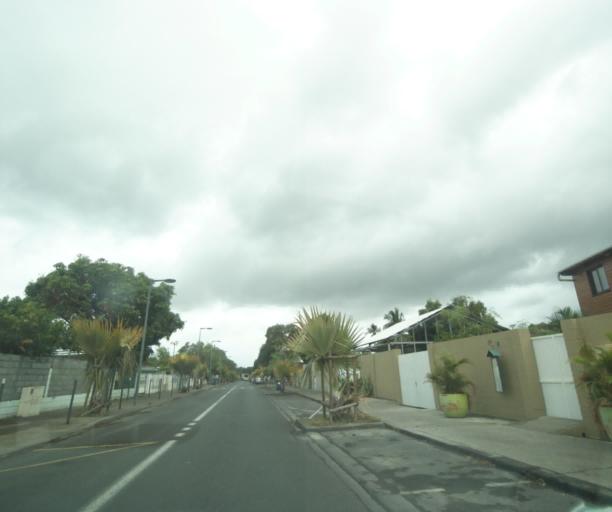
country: RE
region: Reunion
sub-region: Reunion
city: Saint-Paul
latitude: -20.9934
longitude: 55.2850
